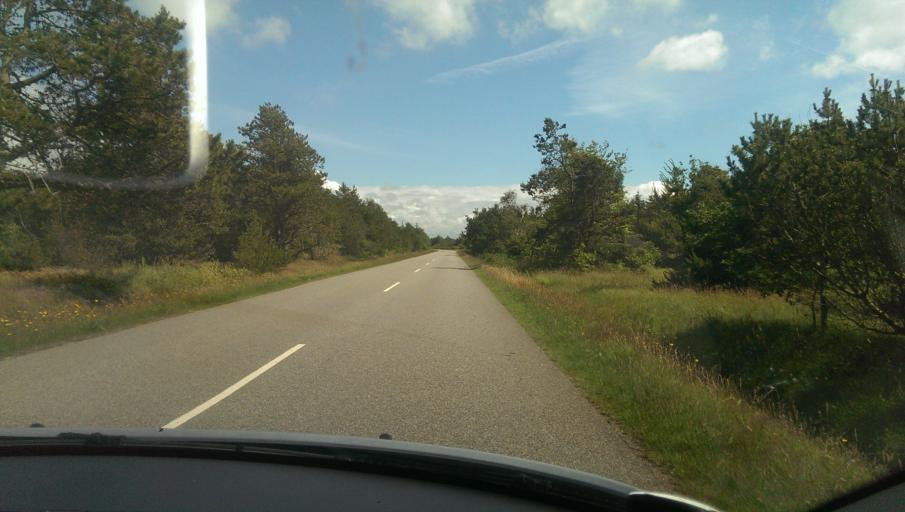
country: DK
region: Central Jutland
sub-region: Ringkobing-Skjern Kommune
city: Ringkobing
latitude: 56.1420
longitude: 8.1462
